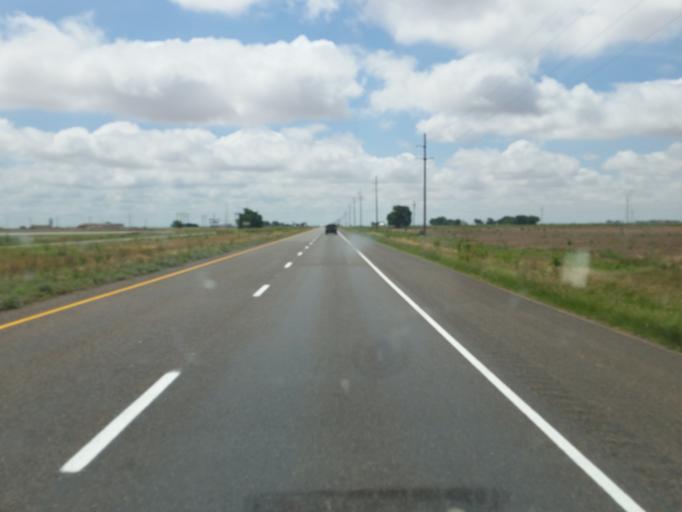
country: US
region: Texas
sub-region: Lubbock County
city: Slaton
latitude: 33.4061
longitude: -101.6214
